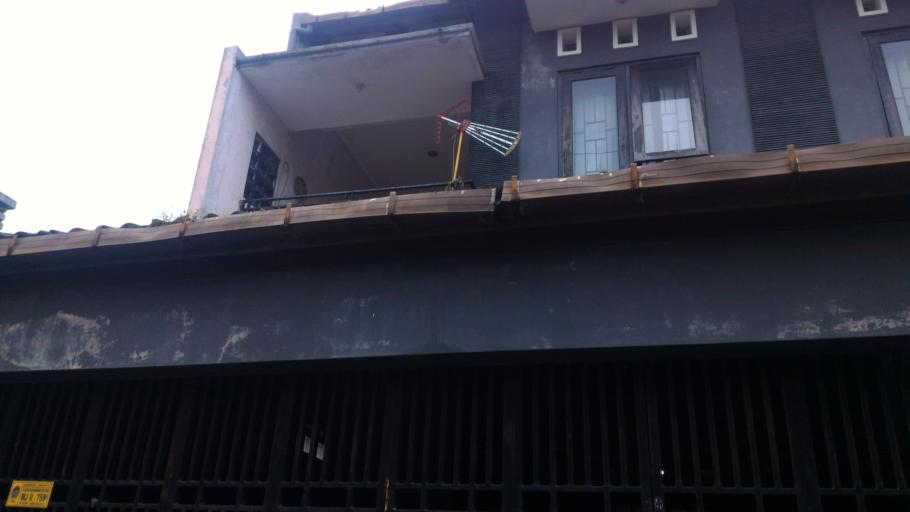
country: ID
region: Daerah Istimewa Yogyakarta
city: Kasihan
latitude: -7.8187
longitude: 110.3592
